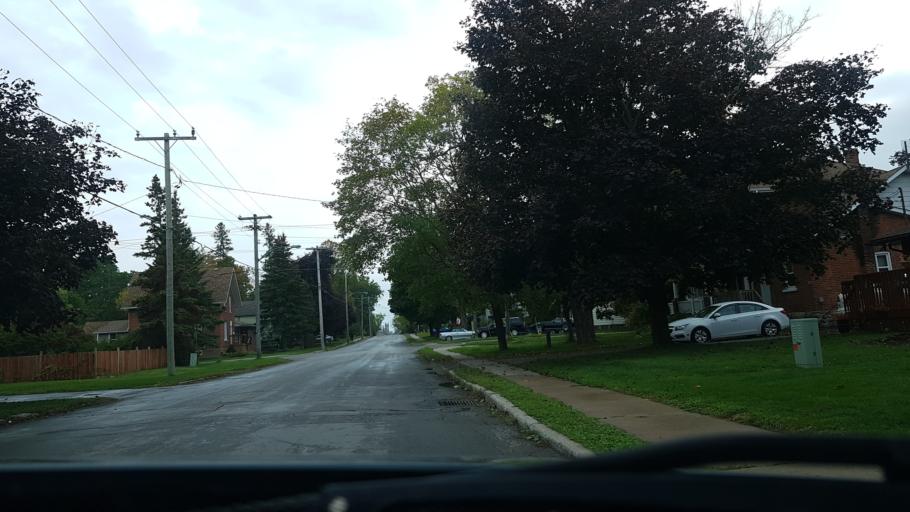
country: CA
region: Ontario
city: Omemee
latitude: 44.3649
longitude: -78.7417
